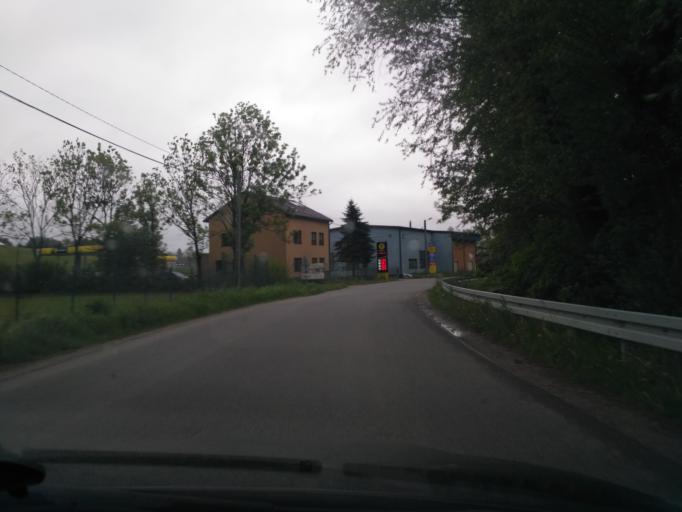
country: PL
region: Subcarpathian Voivodeship
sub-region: Powiat debicki
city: Jodlowa
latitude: 49.8732
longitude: 21.2922
